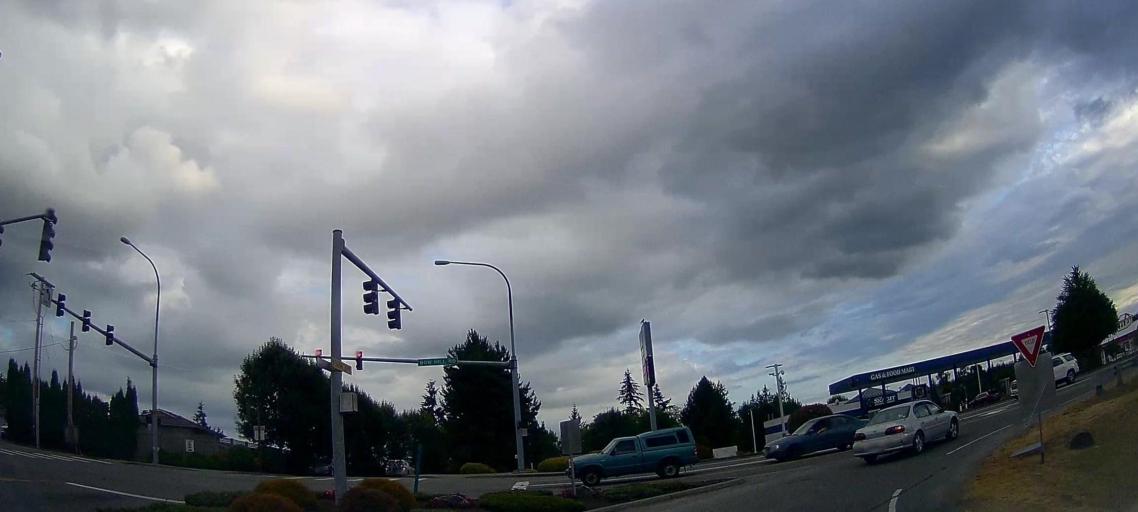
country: US
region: Washington
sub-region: Skagit County
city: Burlington
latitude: 48.5570
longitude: -122.3444
